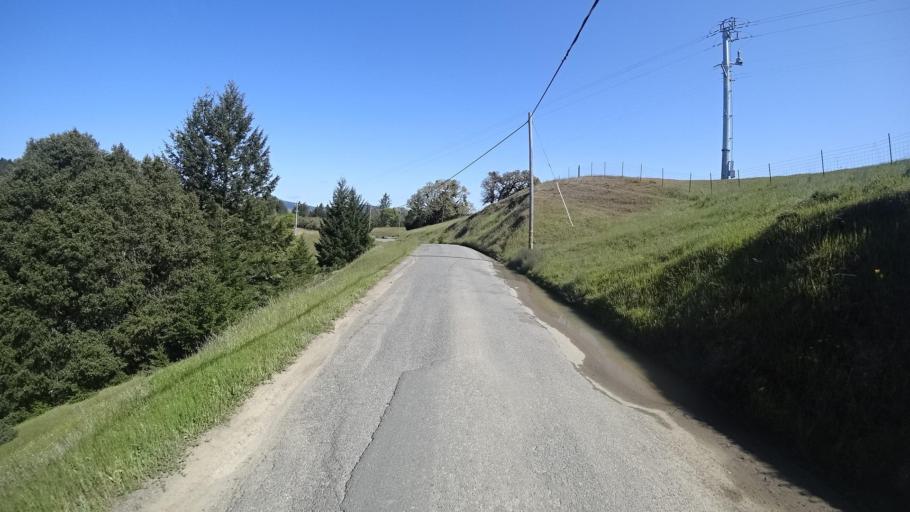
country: US
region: California
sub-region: Humboldt County
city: Redway
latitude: 40.0599
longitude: -123.6417
